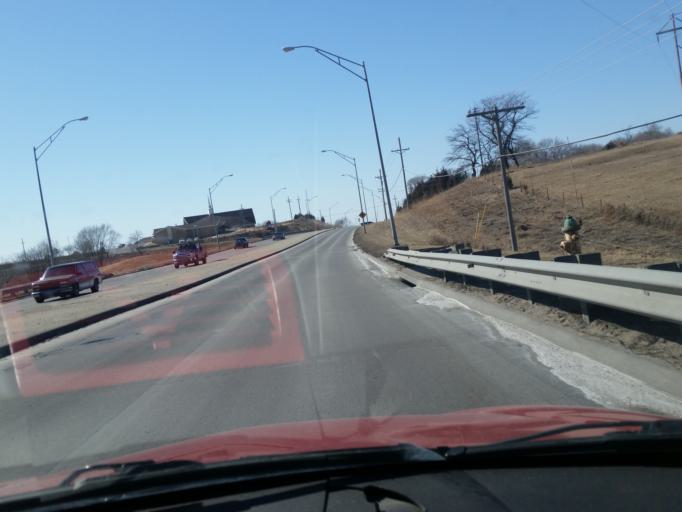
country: US
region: Nebraska
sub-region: Sarpy County
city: Offutt Air Force Base
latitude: 41.1599
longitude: -95.9530
